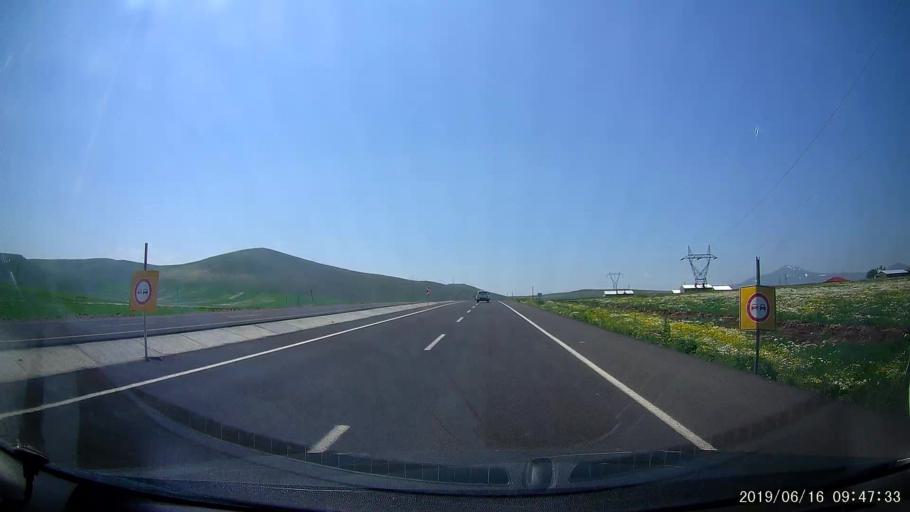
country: TR
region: Kars
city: Digor
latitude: 40.4455
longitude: 43.3452
